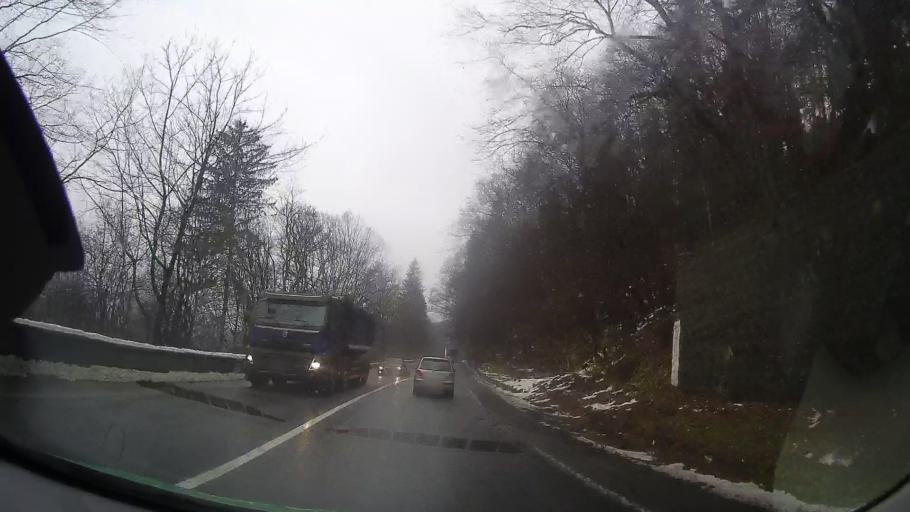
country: RO
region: Neamt
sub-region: Comuna Tarcau
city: Tarcau
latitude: 46.8990
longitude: 26.1195
